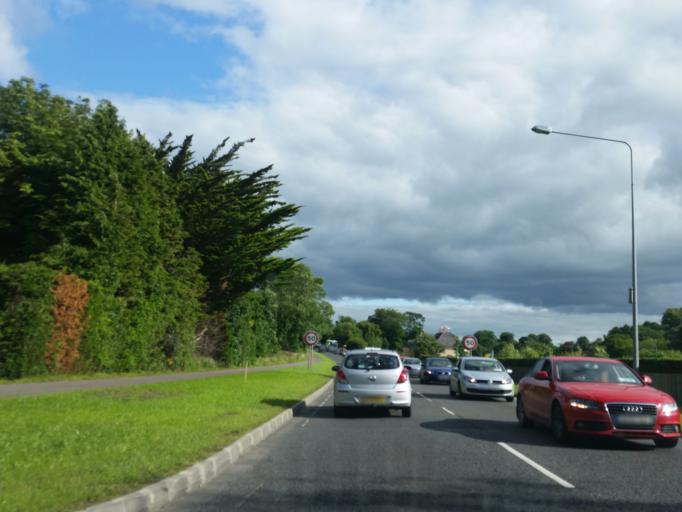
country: GB
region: Northern Ireland
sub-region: Fermanagh District
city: Enniskillen
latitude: 54.3356
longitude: -7.6241
